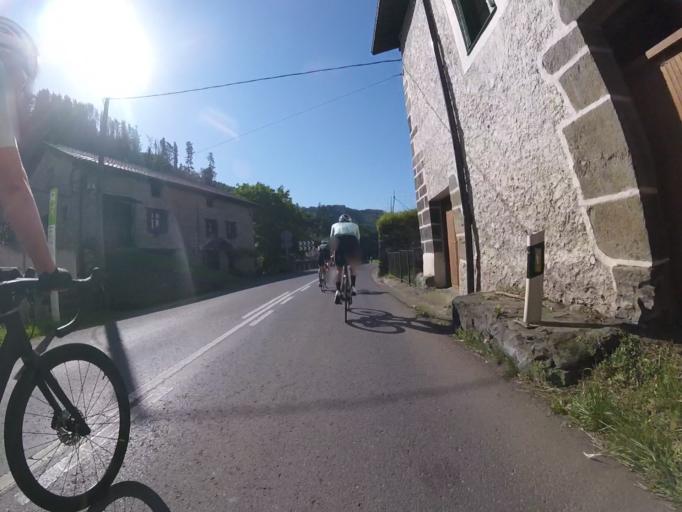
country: ES
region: Basque Country
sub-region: Provincia de Guipuzcoa
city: Beizama
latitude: 43.1508
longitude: -2.2382
